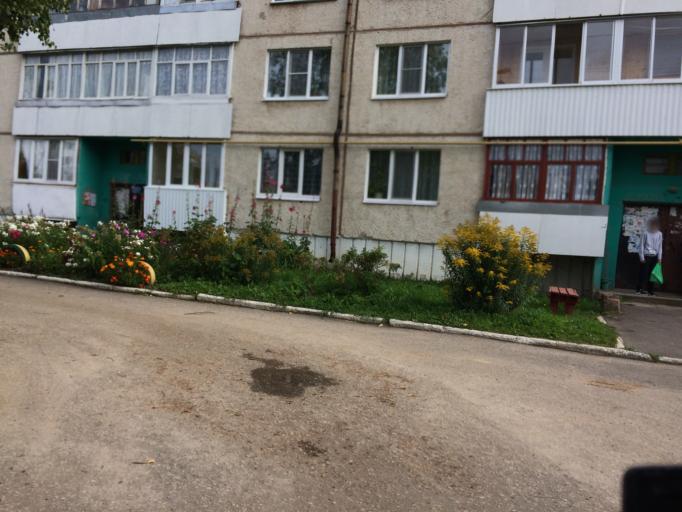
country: RU
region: Mariy-El
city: Yoshkar-Ola
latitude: 56.6502
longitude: 47.9702
